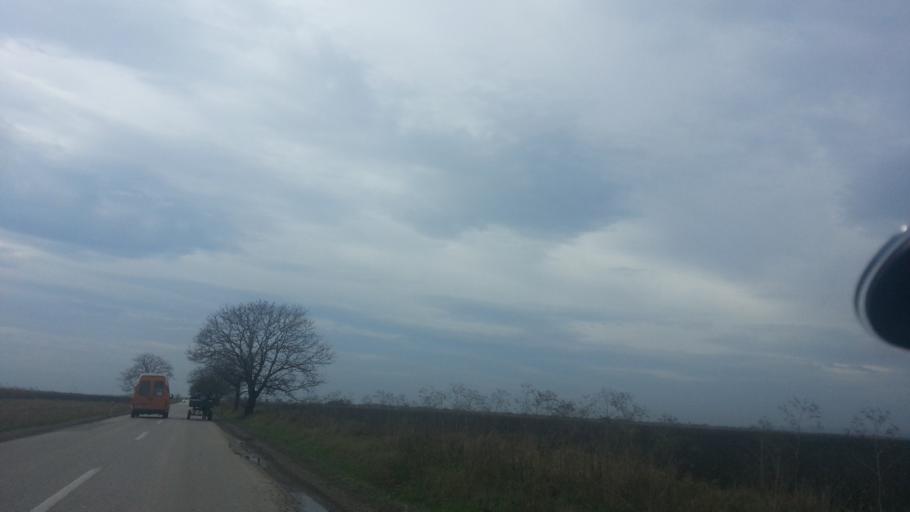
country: RS
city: Golubinci
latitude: 44.9817
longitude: 20.1098
